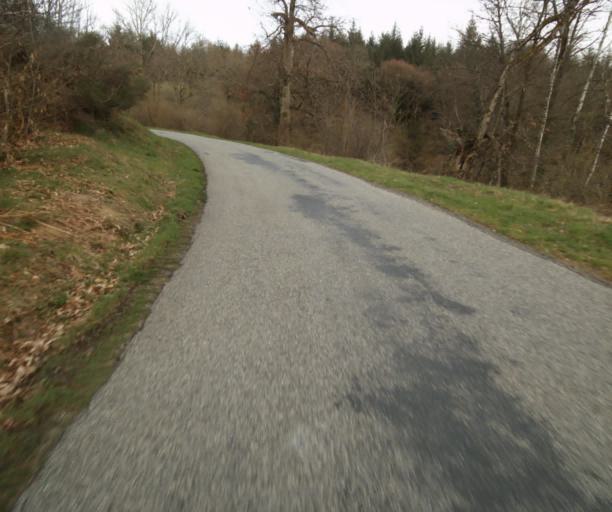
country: FR
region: Limousin
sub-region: Departement de la Correze
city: Saint-Privat
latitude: 45.2258
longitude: 1.9959
